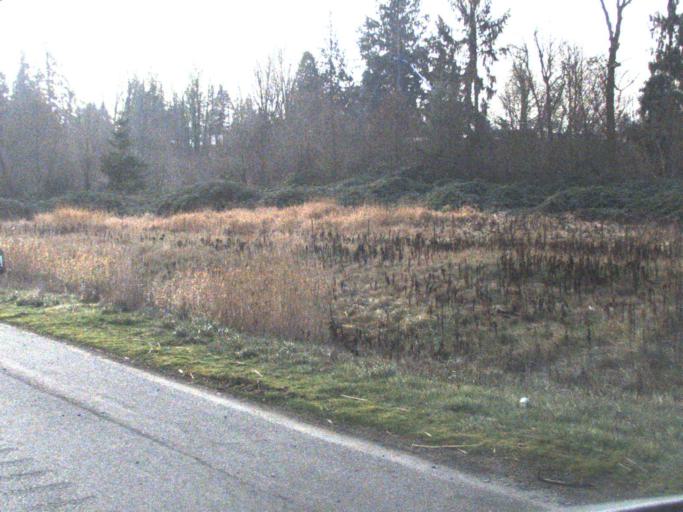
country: US
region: Washington
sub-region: Snohomish County
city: Smokey Point
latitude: 48.1806
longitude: -122.1965
